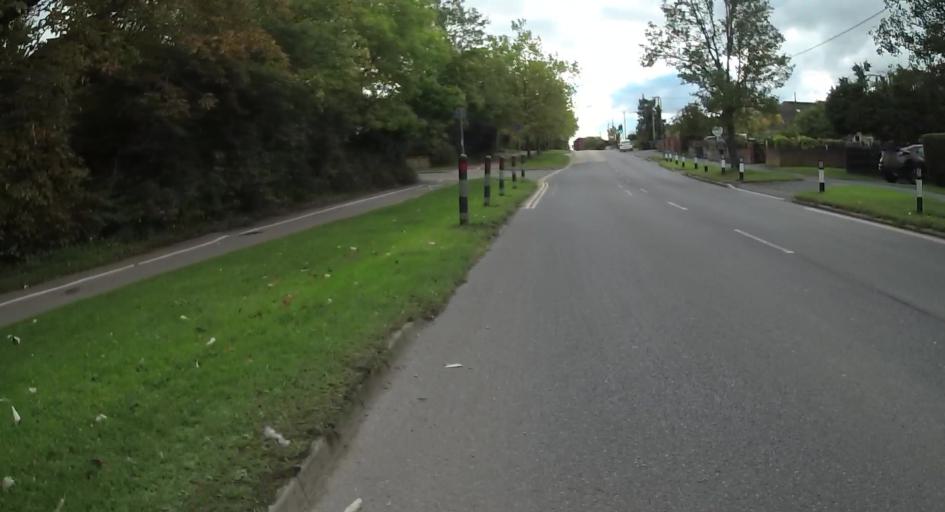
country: GB
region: England
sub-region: Surrey
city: Seale
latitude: 51.2418
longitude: -0.7294
